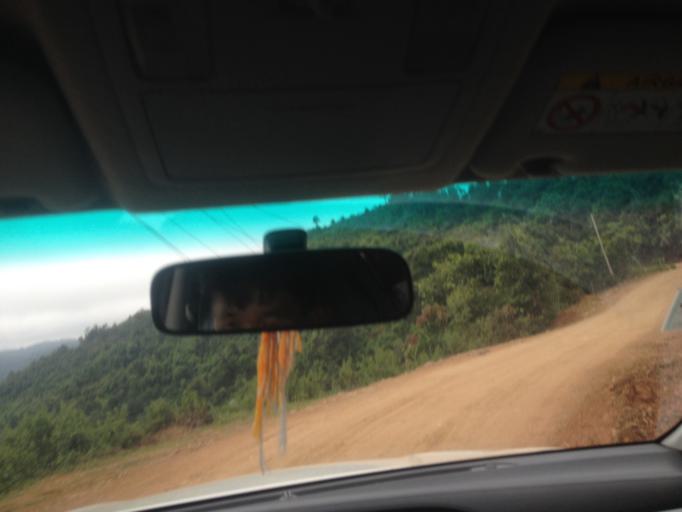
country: TH
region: Nan
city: Chaloem Phra Kiat
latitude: 19.9896
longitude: 101.1409
